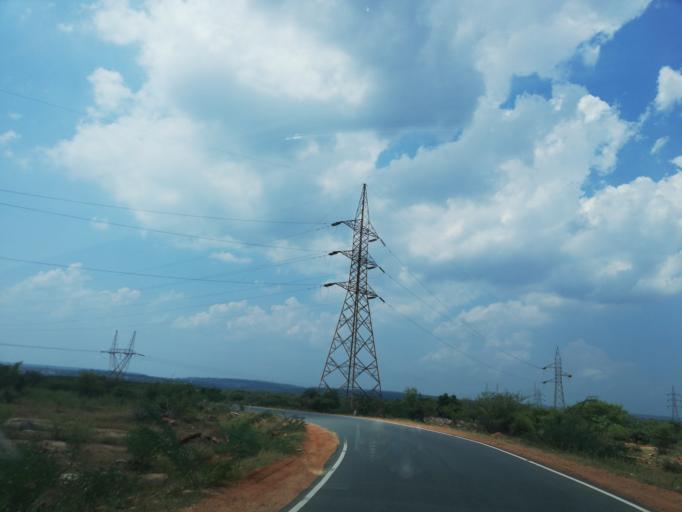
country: IN
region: Andhra Pradesh
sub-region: Guntur
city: Macherla
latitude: 16.5673
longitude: 79.3473
